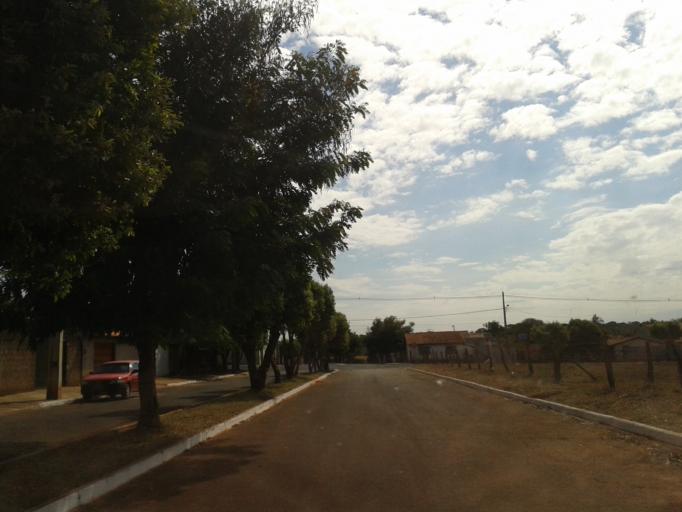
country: BR
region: Minas Gerais
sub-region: Santa Vitoria
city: Santa Vitoria
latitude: -18.8388
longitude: -50.1182
